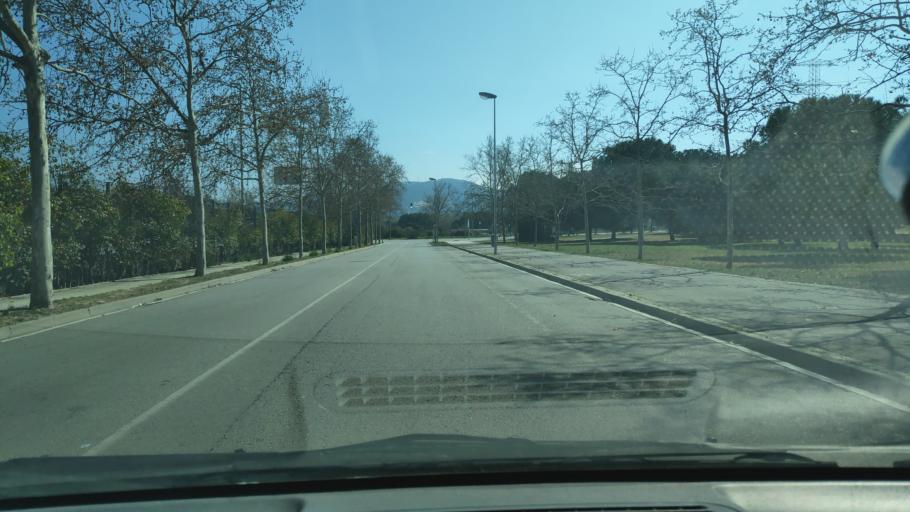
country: ES
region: Catalonia
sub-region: Provincia de Barcelona
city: Santa Perpetua de Mogoda
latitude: 41.5319
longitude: 2.1911
